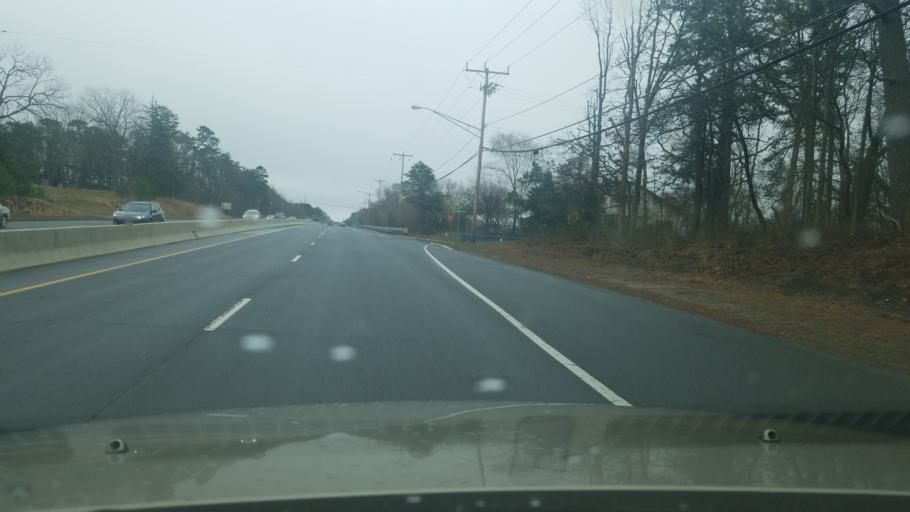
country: US
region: New Jersey
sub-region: Ocean County
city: Leisure Knoll
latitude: 40.0041
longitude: -74.2951
